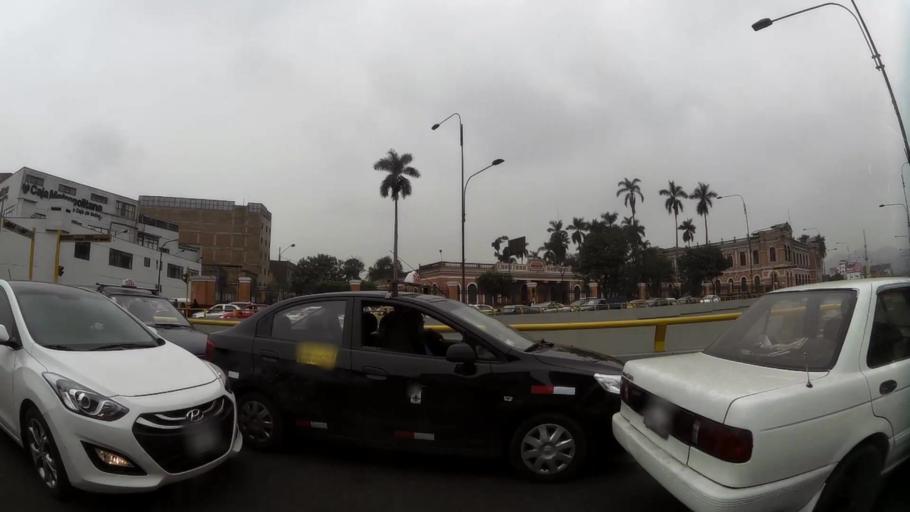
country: PE
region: Lima
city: Lima
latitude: -12.0584
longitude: -77.0242
